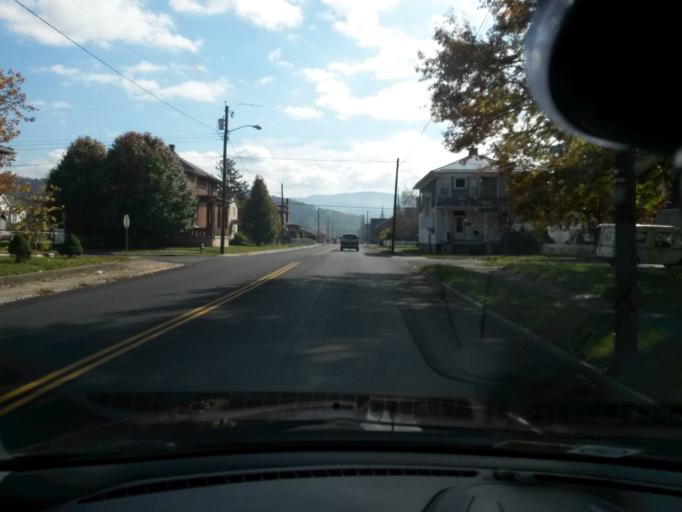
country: US
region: Virginia
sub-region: City of Covington
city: Covington
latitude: 37.7905
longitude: -79.9909
